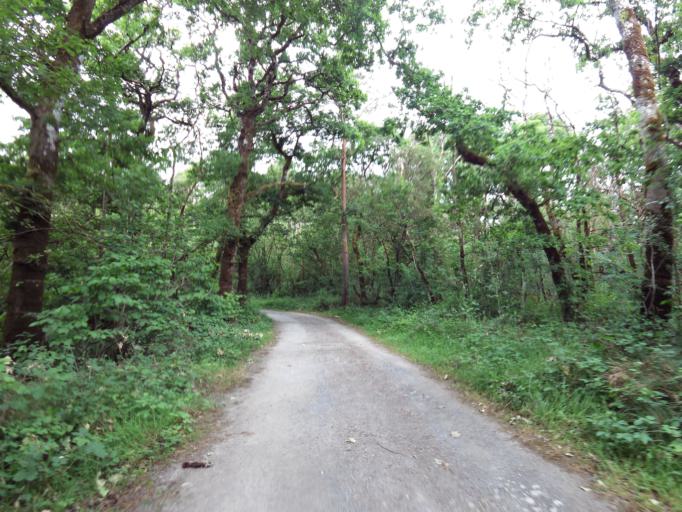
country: IE
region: Connaught
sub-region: County Galway
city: Gort
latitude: 53.0783
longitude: -8.8554
